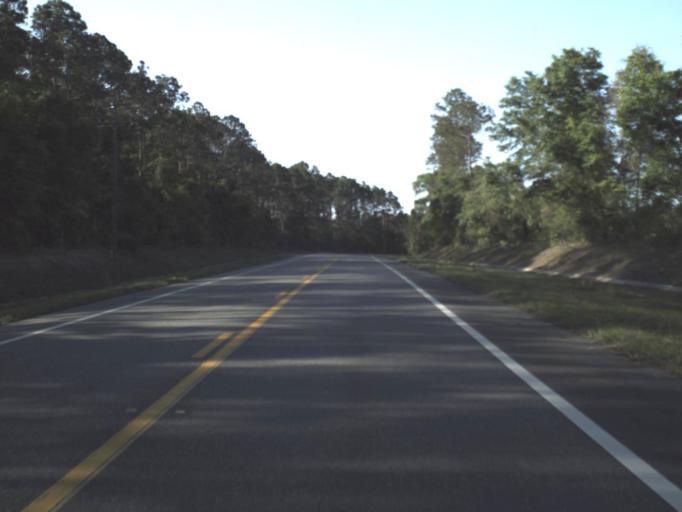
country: US
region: Florida
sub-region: Liberty County
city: Bristol
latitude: 30.4130
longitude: -84.7845
